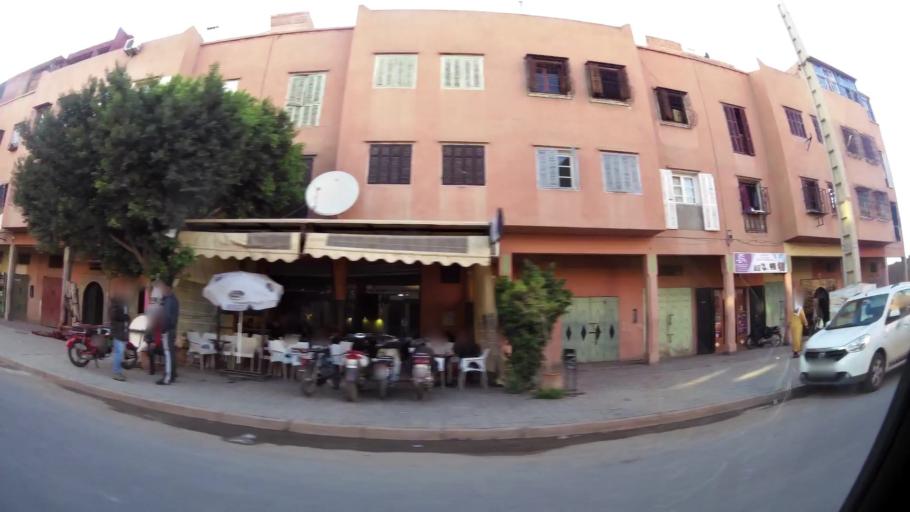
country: MA
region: Marrakech-Tensift-Al Haouz
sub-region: Marrakech
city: Marrakesh
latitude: 31.6185
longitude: -8.0552
